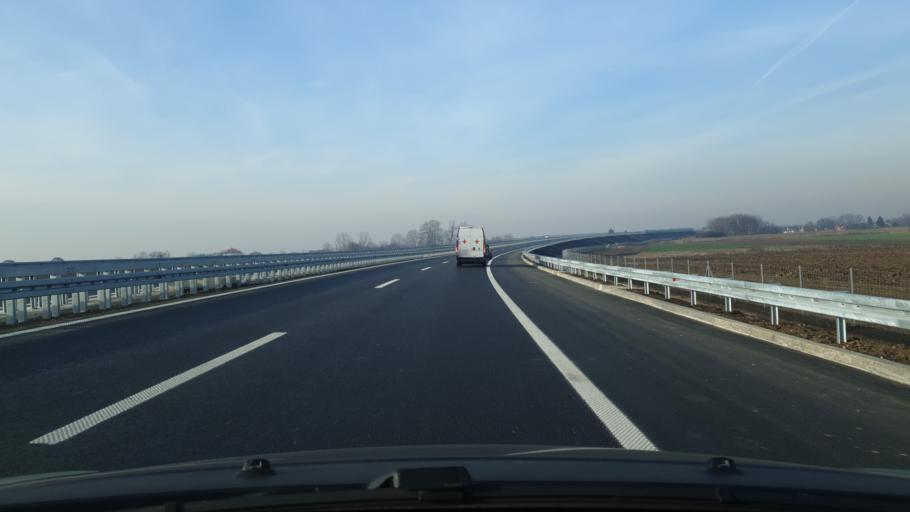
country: RS
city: Boljevci
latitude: 44.7276
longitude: 20.2497
